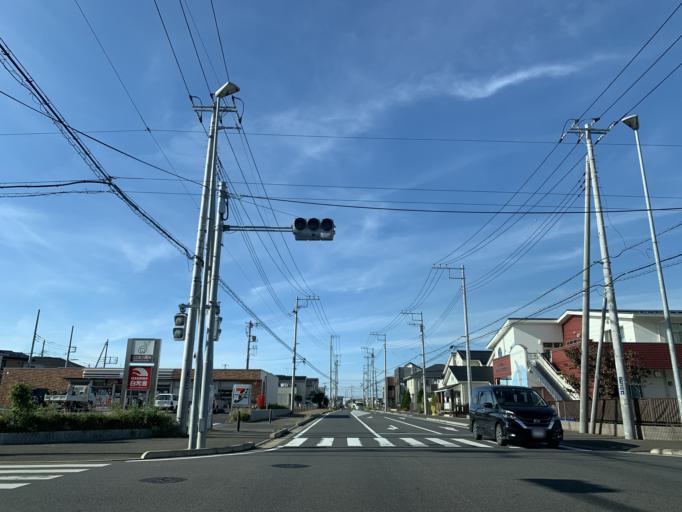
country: JP
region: Chiba
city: Nagareyama
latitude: 35.8794
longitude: 139.9266
